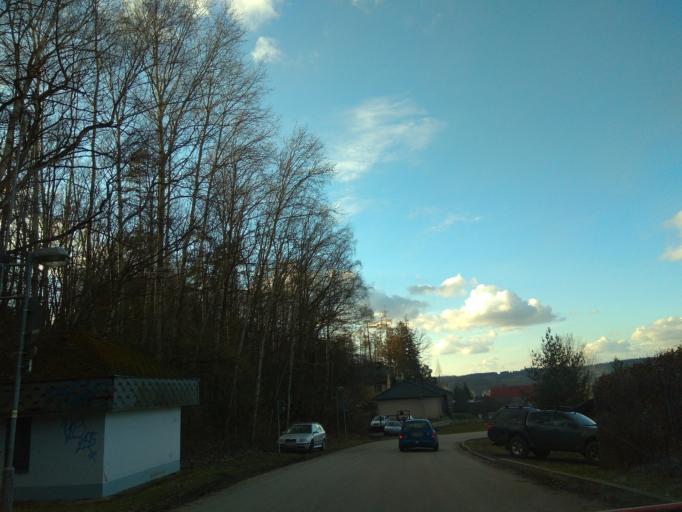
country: CZ
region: Jihocesky
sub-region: Okres Ceske Budejovice
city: Hluboka nad Vltavou
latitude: 49.0513
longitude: 14.4613
